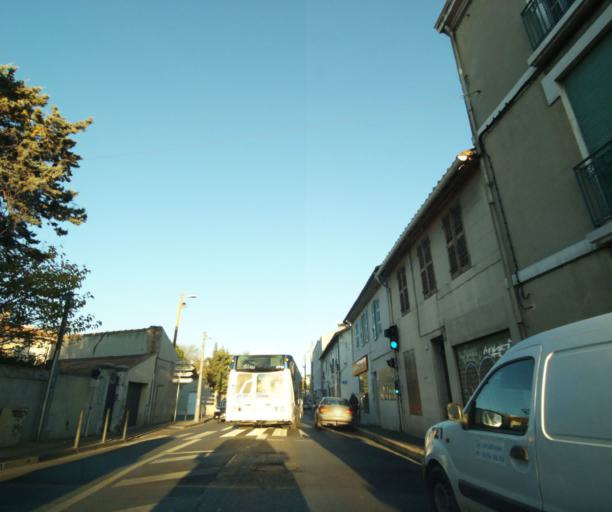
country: FR
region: Provence-Alpes-Cote d'Azur
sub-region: Departement des Bouches-du-Rhone
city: Marseille 04
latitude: 43.3051
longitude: 5.4166
